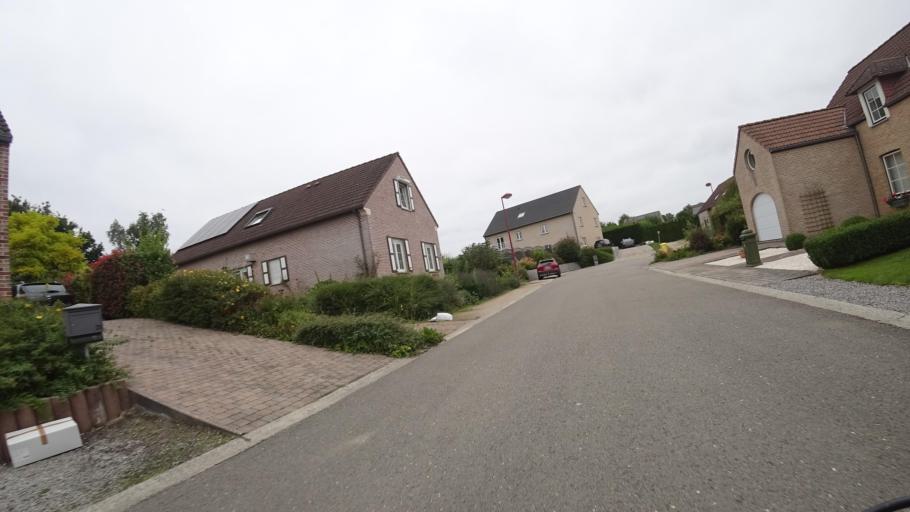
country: BE
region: Wallonia
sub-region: Province du Brabant Wallon
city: Mont-Saint-Guibert
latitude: 50.6369
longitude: 4.6253
